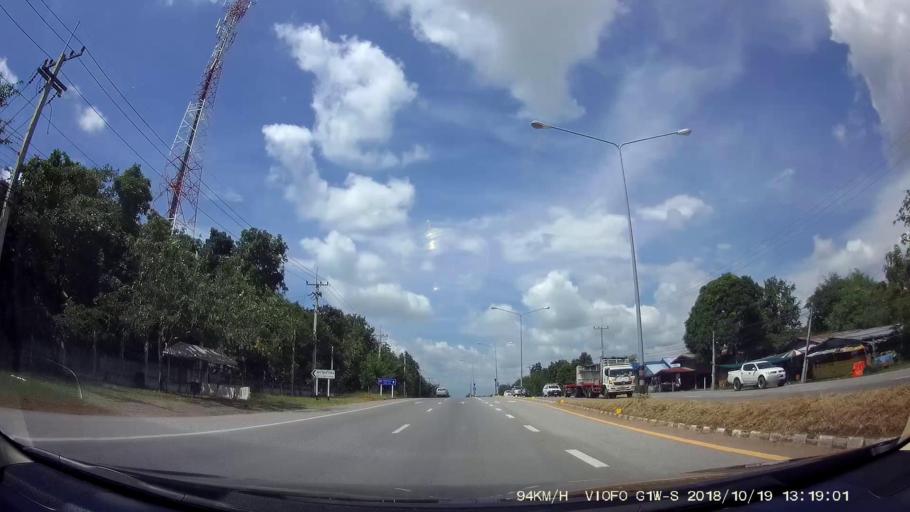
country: TH
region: Chaiyaphum
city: Chatturat
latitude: 15.4231
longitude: 101.8321
